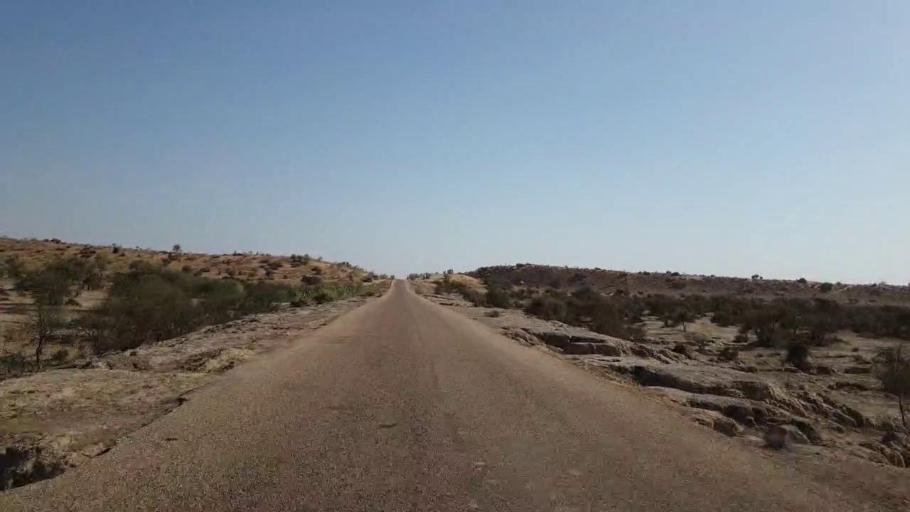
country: PK
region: Sindh
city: Nabisar
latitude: 25.0832
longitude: 70.0418
